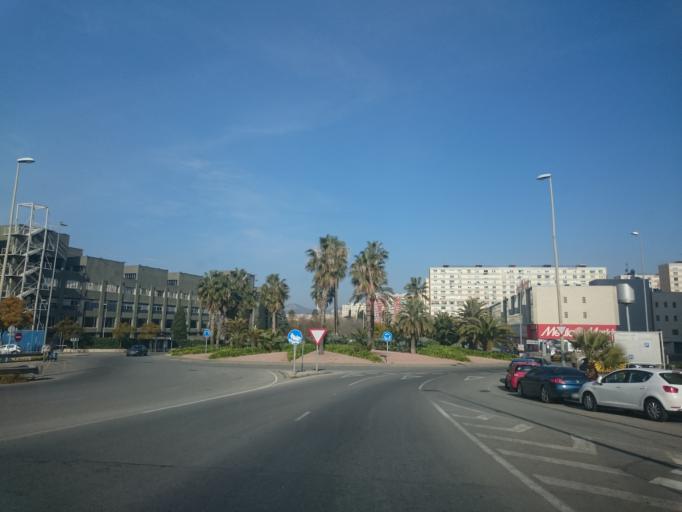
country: ES
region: Catalonia
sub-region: Provincia de Barcelona
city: L'Hospitalet de Llobregat
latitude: 41.3454
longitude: 2.1080
